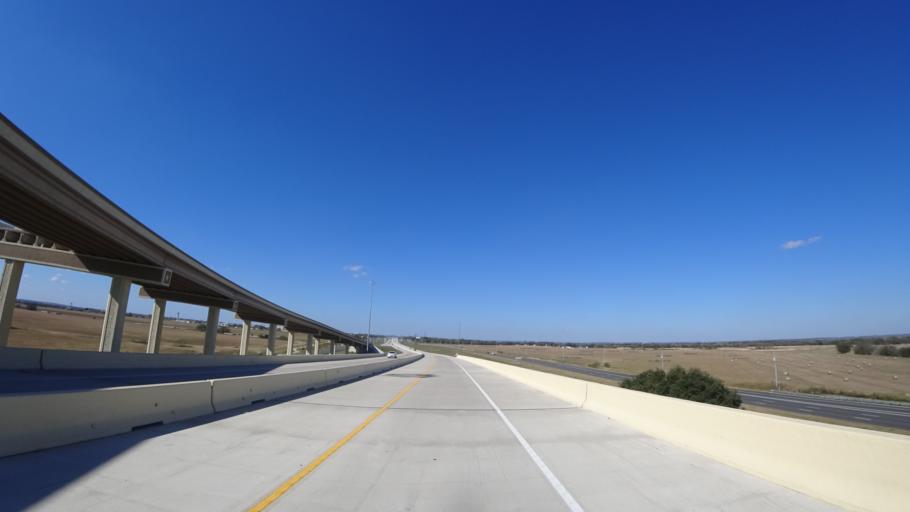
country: US
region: Texas
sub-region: Travis County
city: Hornsby Bend
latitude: 30.1964
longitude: -97.6268
